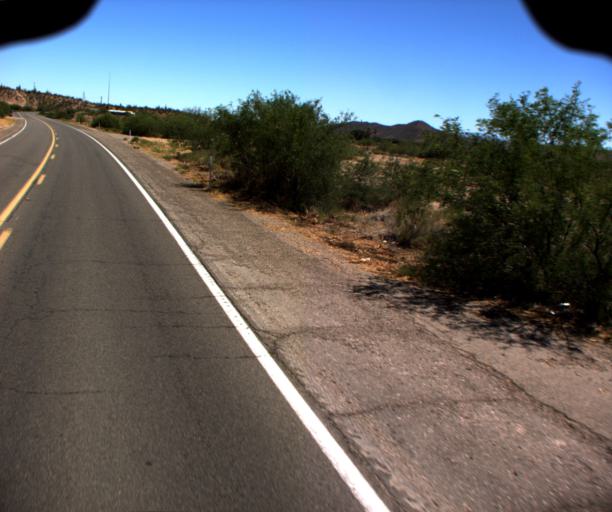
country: US
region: Arizona
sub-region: Pinal County
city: Kearny
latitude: 32.9420
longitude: -110.7404
